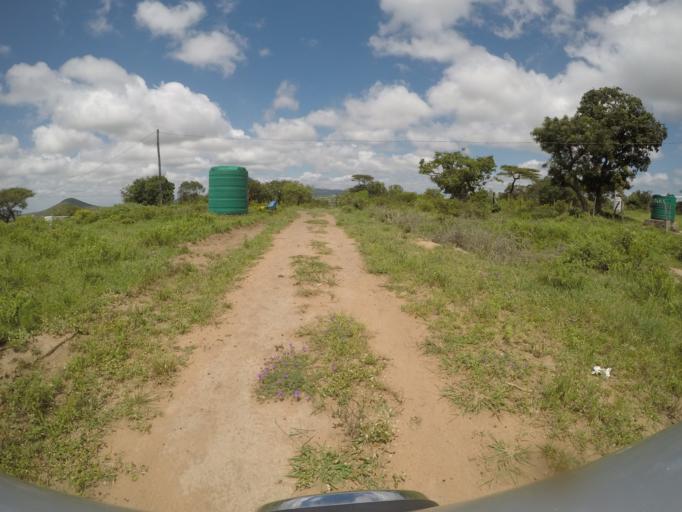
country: ZA
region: KwaZulu-Natal
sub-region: uThungulu District Municipality
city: Empangeni
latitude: -28.5852
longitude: 31.8308
